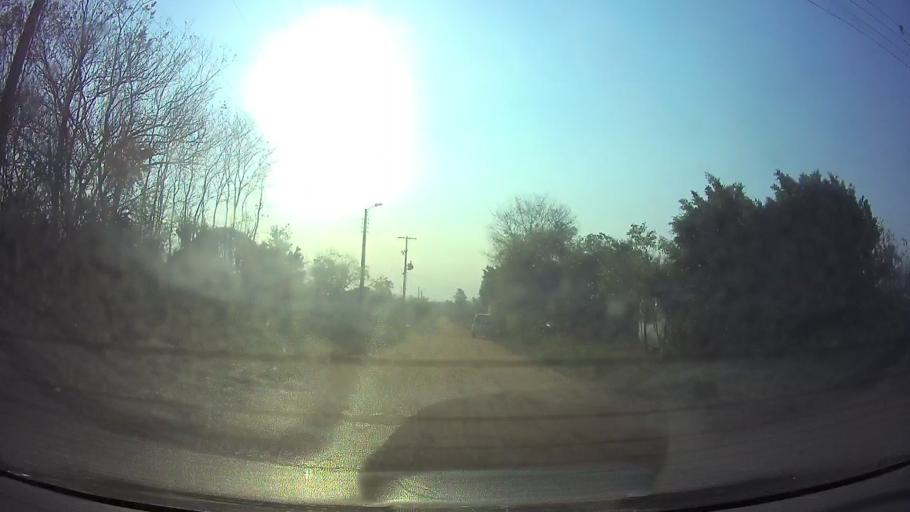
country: PY
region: Central
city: Limpio
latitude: -25.2193
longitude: -57.4866
